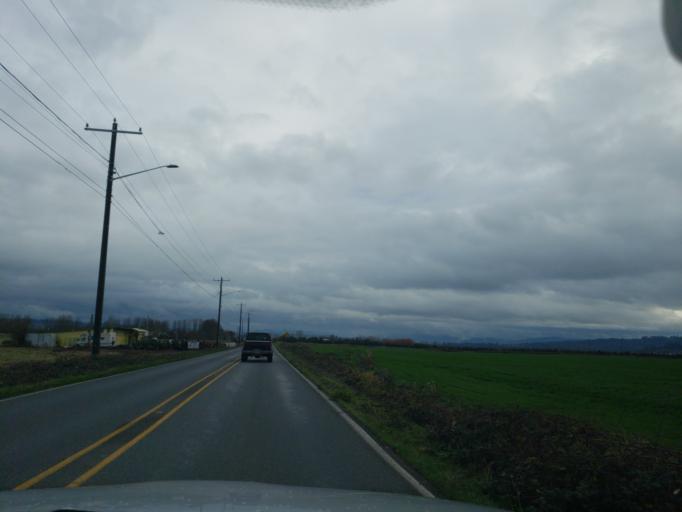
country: US
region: Washington
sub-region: Snohomish County
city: Silver Firs
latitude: 47.8993
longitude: -122.1352
